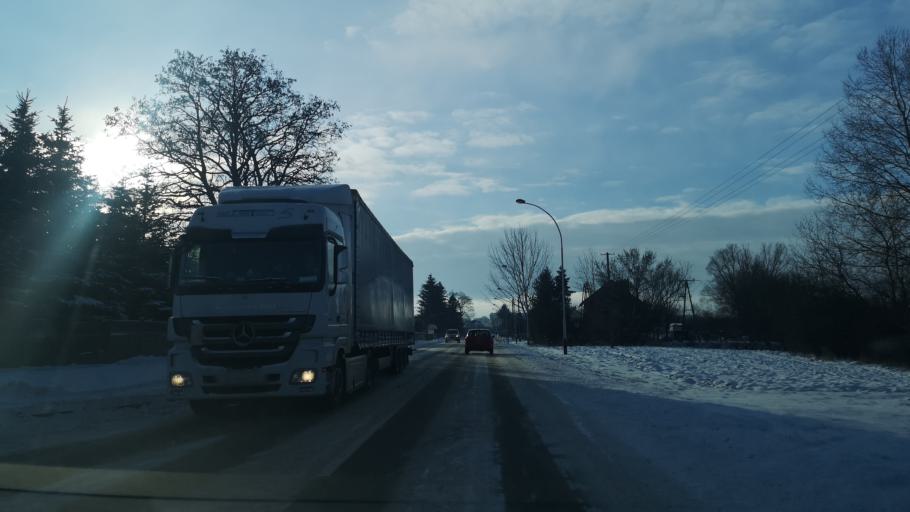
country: PL
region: Subcarpathian Voivodeship
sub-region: Powiat przeworski
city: Gorliczyna
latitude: 50.0780
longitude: 22.4934
